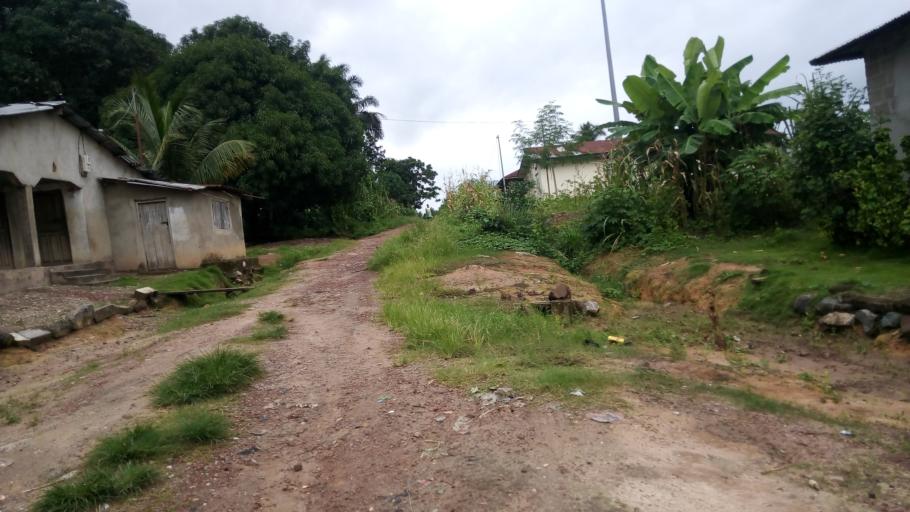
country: SL
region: Northern Province
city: Lunsar
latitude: 8.6894
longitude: -12.5356
